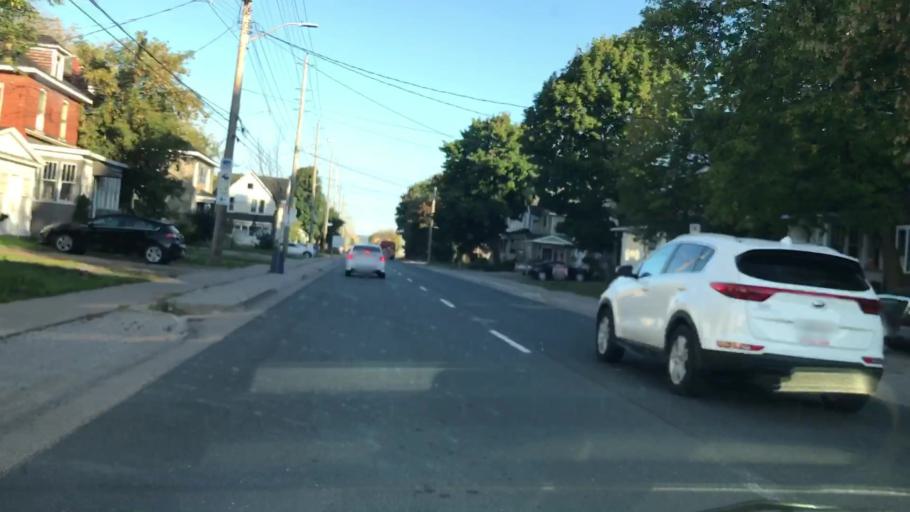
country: CA
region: Ontario
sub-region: Algoma
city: Sault Ste. Marie
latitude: 46.5133
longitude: -84.3304
